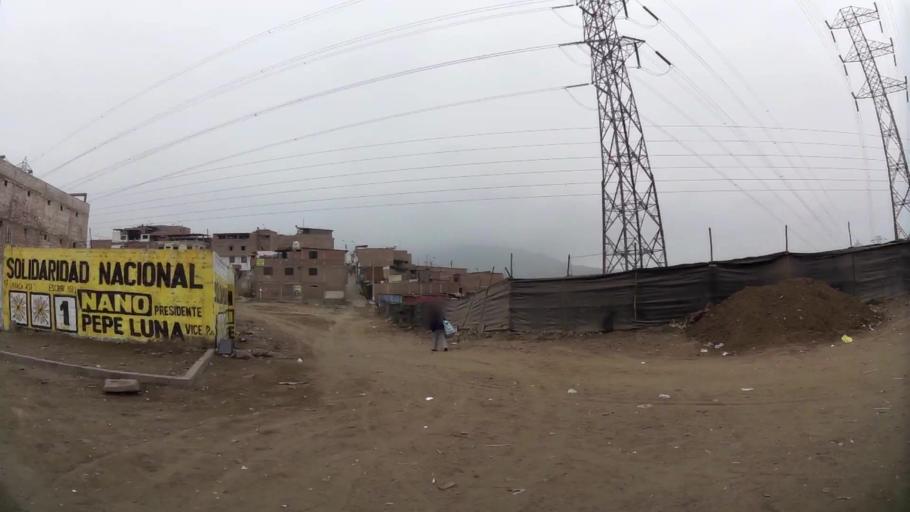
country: PE
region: Lima
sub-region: Lima
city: Surco
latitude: -12.2291
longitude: -76.9107
